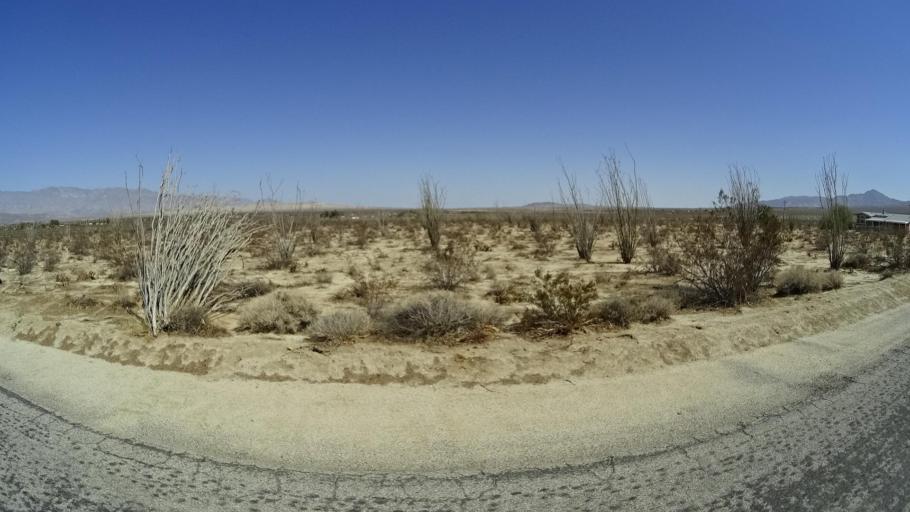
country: US
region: California
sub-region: San Diego County
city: Borrego Springs
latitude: 33.2225
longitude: -116.3652
